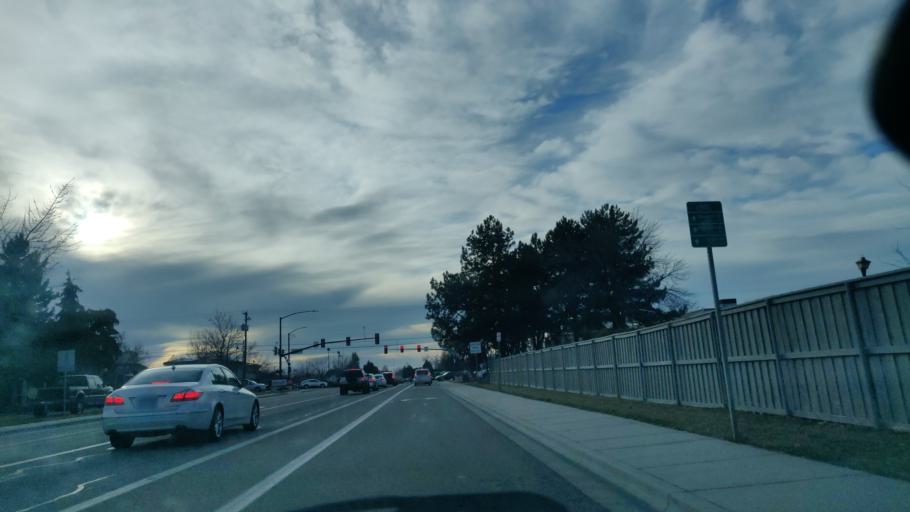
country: US
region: Idaho
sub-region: Ada County
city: Garden City
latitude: 43.6123
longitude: -116.2727
